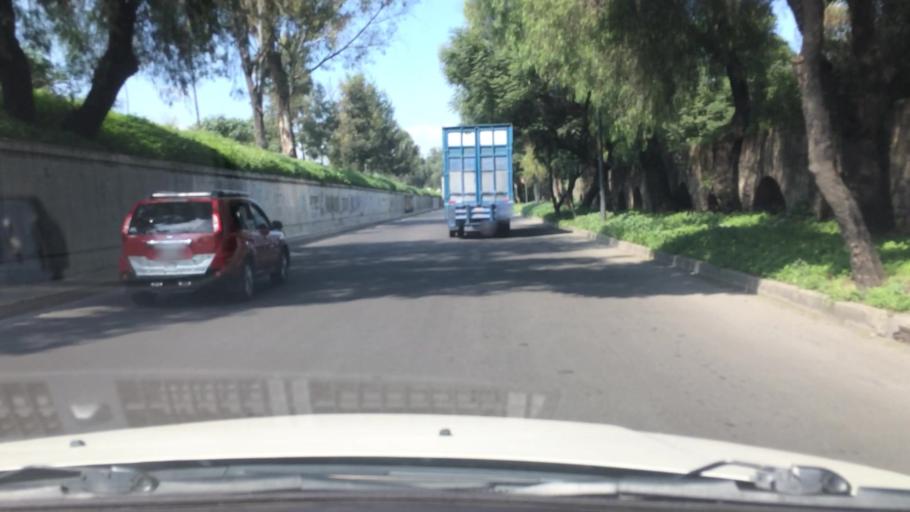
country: MX
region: Mexico
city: Colonia Lindavista
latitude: 19.5219
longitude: -99.1498
